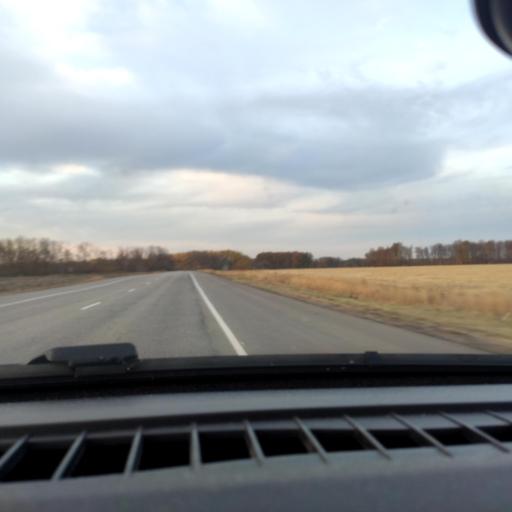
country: RU
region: Voronezj
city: Devitsa
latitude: 51.5883
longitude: 38.9771
